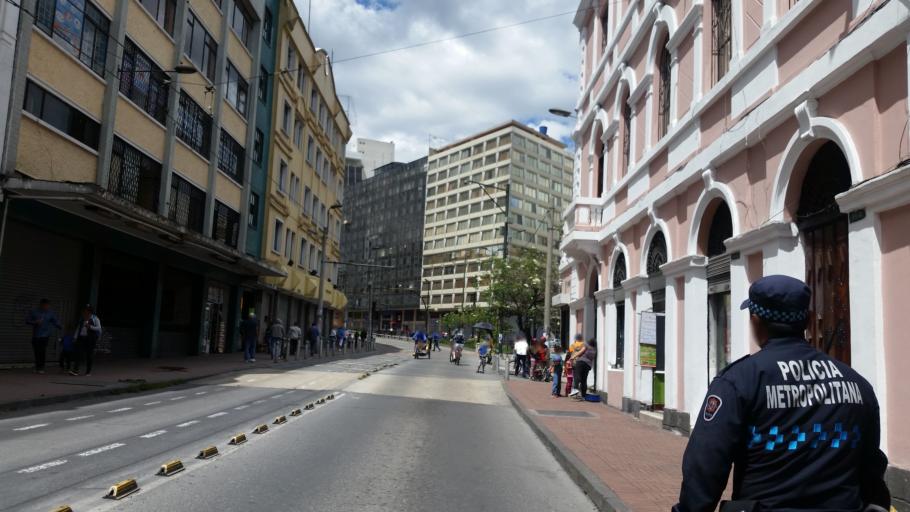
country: EC
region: Pichincha
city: Quito
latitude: -0.2177
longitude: -78.5065
